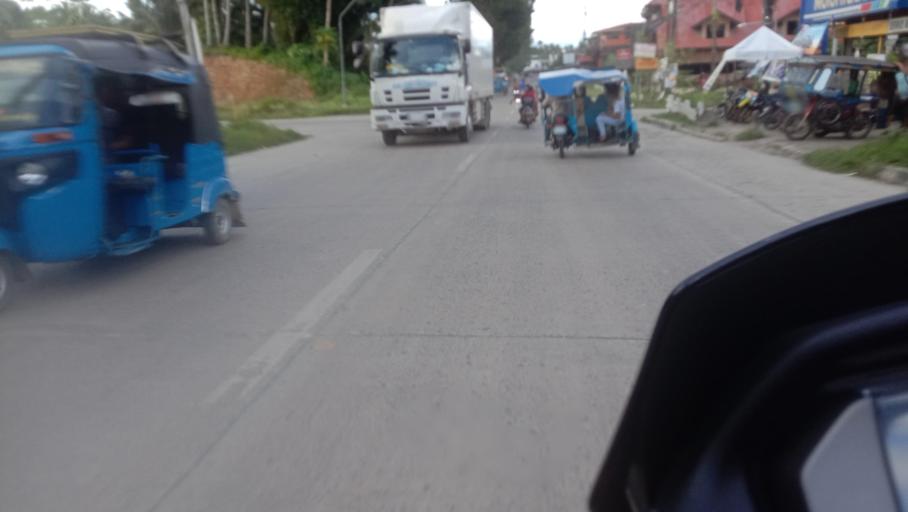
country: PH
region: Caraga
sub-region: Province of Surigao del Sur
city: Barobo
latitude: 8.5306
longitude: 126.1202
